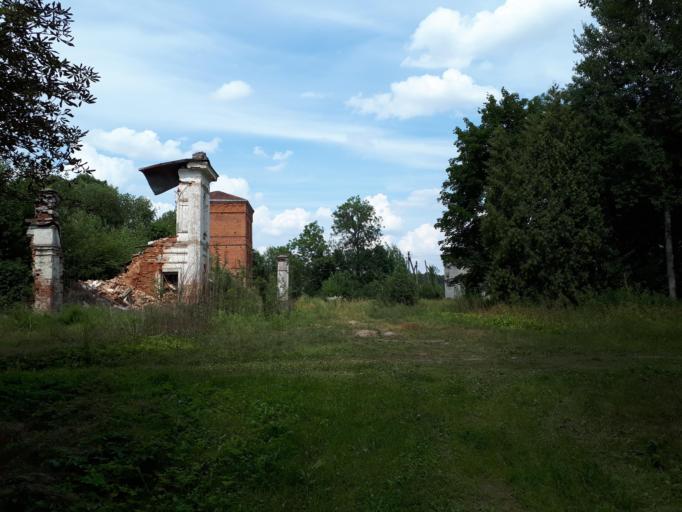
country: LT
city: Kupiskis
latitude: 55.6366
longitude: 24.8798
